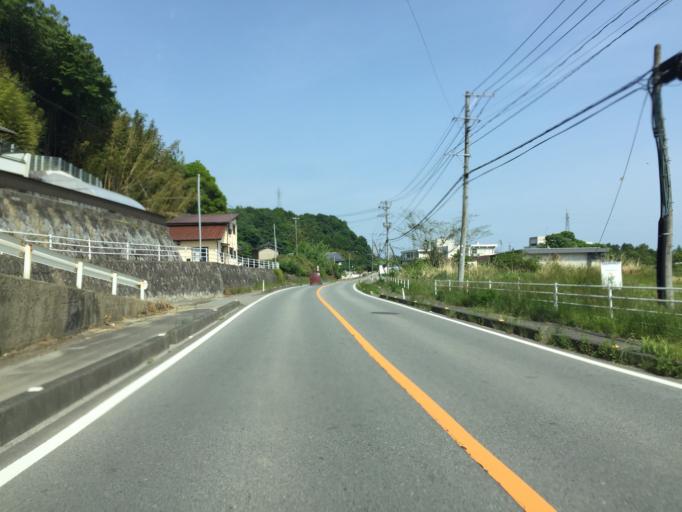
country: JP
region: Ibaraki
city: Kitaibaraki
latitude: 36.9295
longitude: 140.7702
